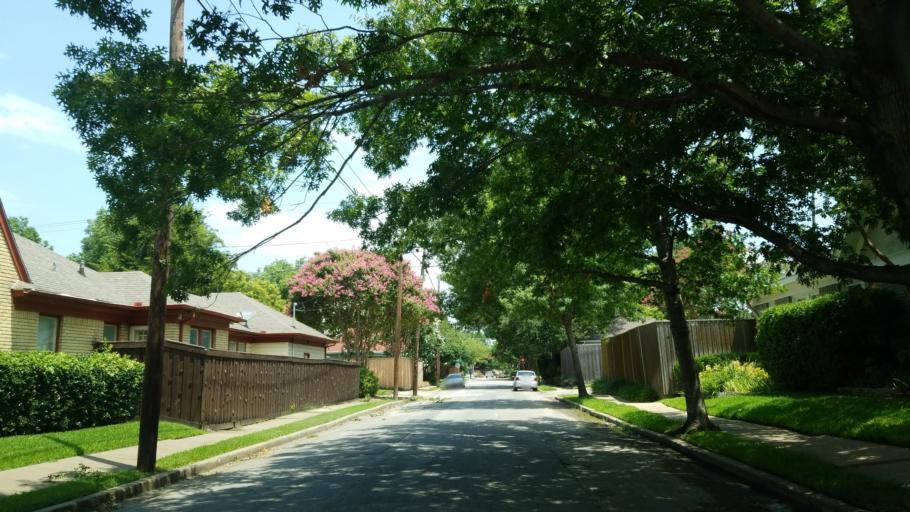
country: US
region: Texas
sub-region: Dallas County
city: Highland Park
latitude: 32.8255
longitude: -96.7823
